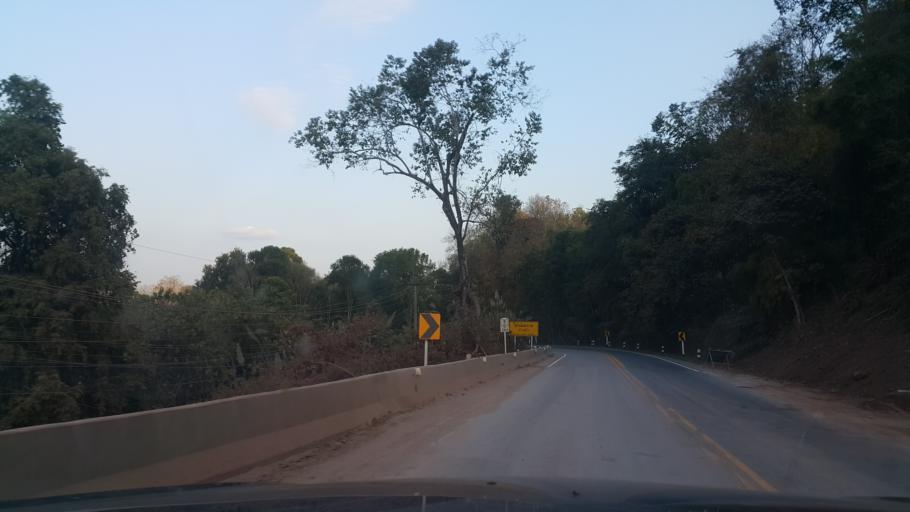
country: TH
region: Loei
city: Phu Ruea
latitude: 17.4631
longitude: 101.5247
